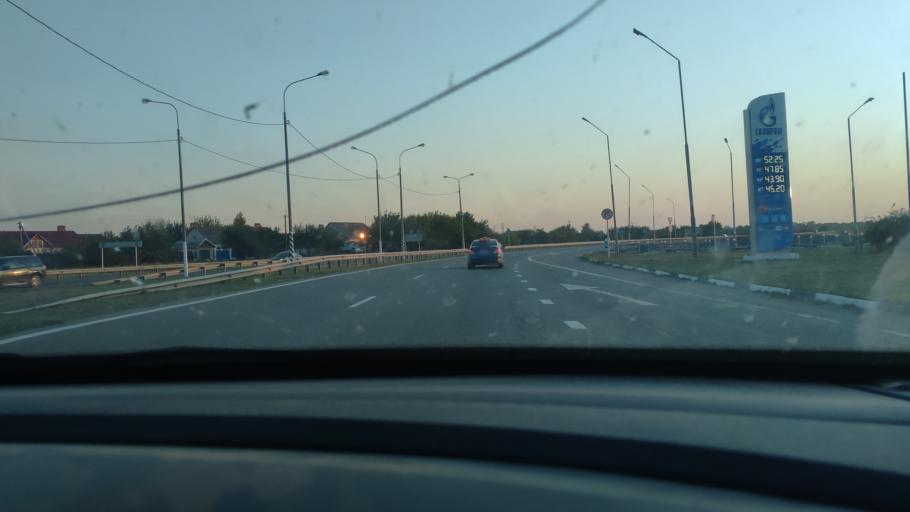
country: RU
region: Krasnodarskiy
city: Timashevsk
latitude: 45.6073
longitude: 38.9849
